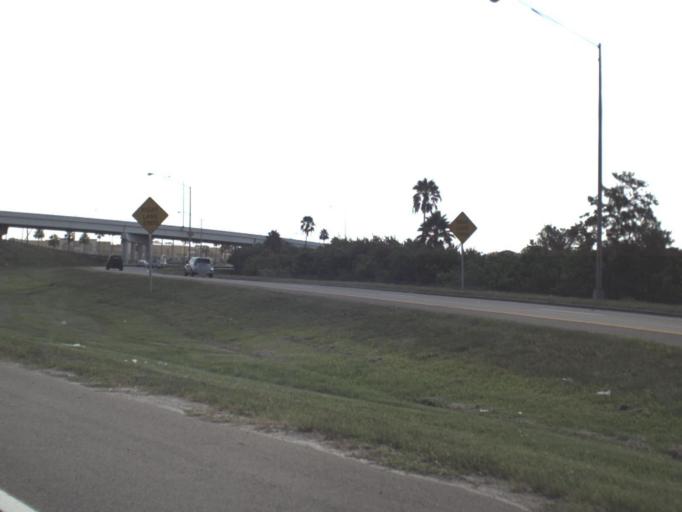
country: US
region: Florida
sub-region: Pinellas County
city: Bay Pines
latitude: 27.8135
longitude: -82.7870
